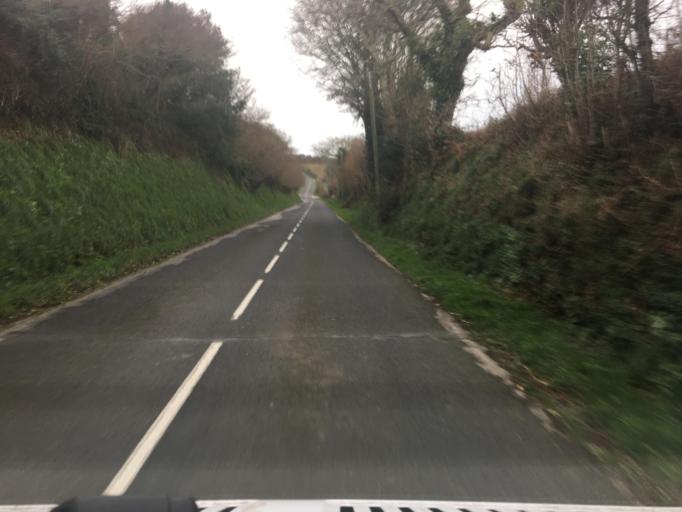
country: FR
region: Lower Normandy
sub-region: Departement de la Manche
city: Beaumont-Hague
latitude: 49.6811
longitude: -1.8505
